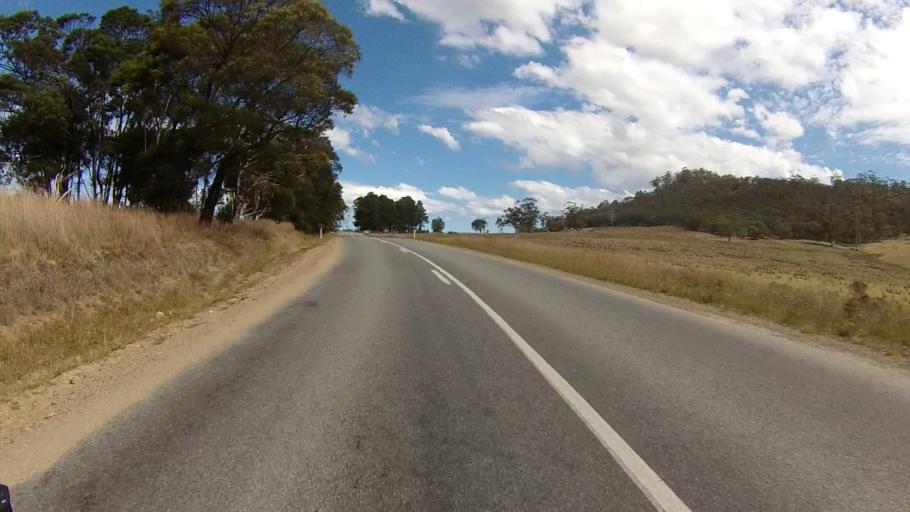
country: AU
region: Tasmania
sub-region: Break O'Day
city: St Helens
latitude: -41.9666
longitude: 148.1520
